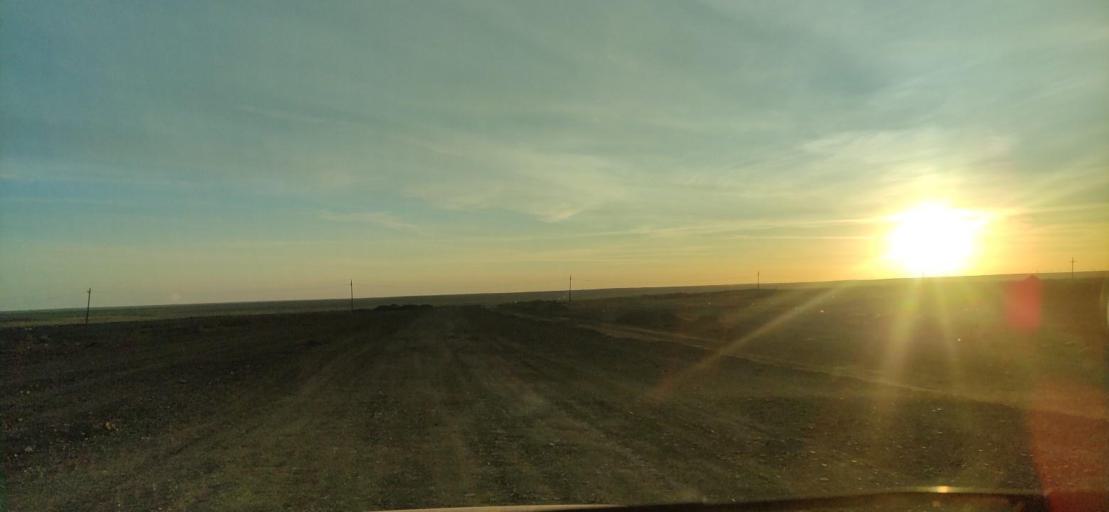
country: KZ
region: Qaraghandy
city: Saryshaghan
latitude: 46.0089
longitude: 73.5864
